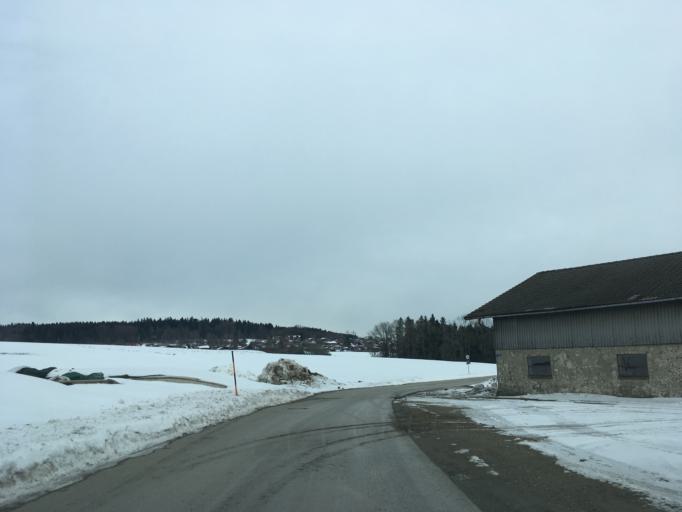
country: DE
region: Bavaria
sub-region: Upper Bavaria
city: Schnaitsee
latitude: 48.0632
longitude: 12.3557
